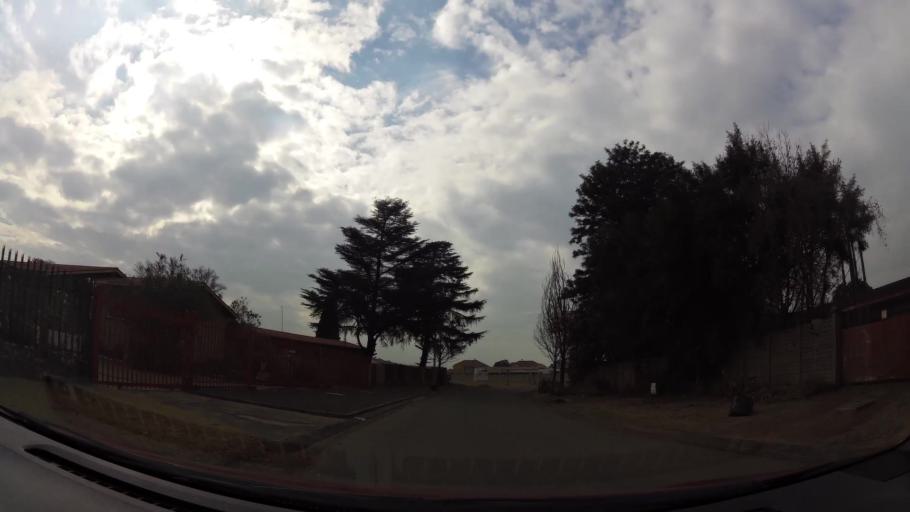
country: ZA
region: Gauteng
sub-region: Sedibeng District Municipality
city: Vanderbijlpark
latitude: -26.6798
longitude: 27.8373
